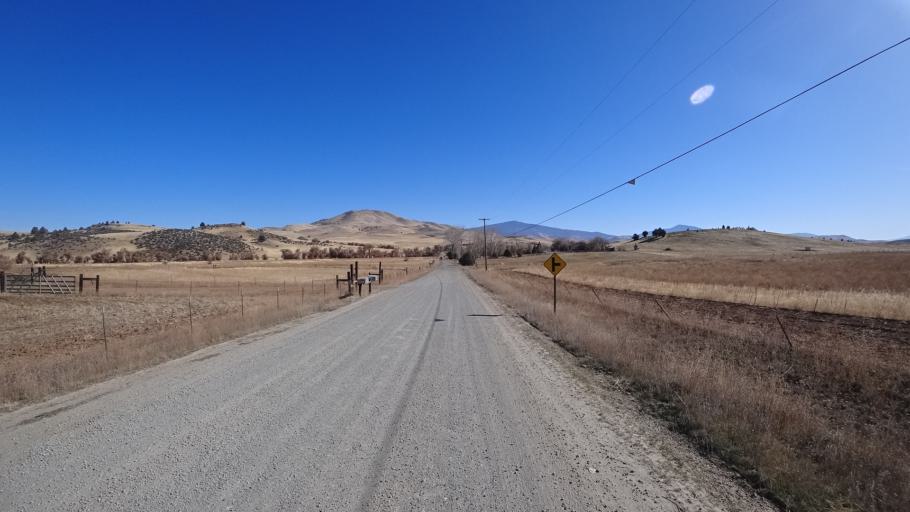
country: US
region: California
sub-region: Siskiyou County
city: Montague
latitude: 41.8478
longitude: -122.4613
